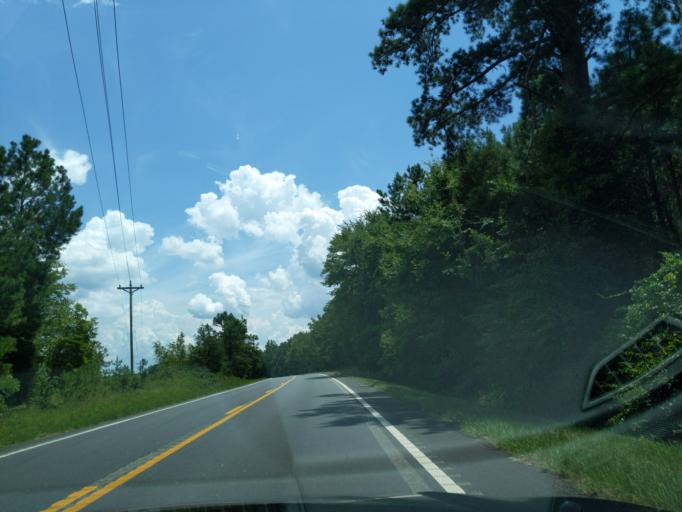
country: US
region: South Carolina
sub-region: Edgefield County
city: Edgefield
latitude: 33.8534
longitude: -81.9820
